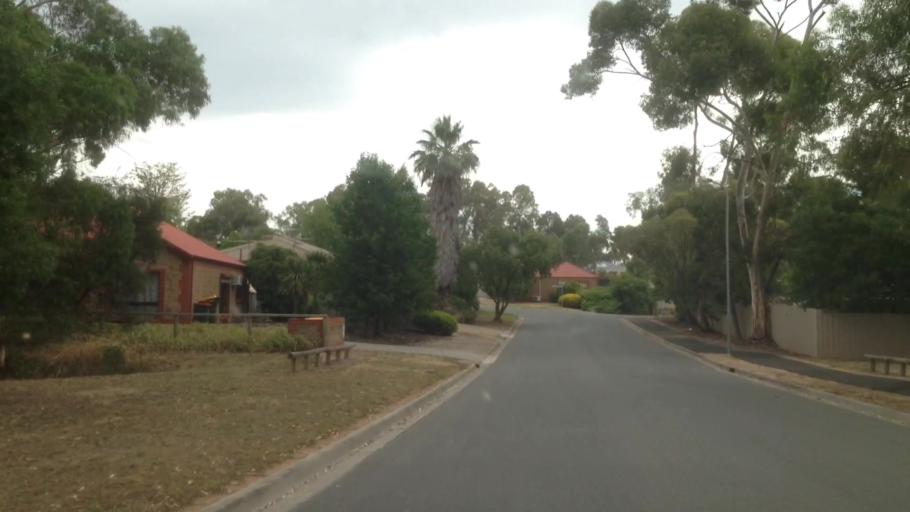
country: AU
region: South Australia
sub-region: Barossa
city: Williamstown
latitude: -34.6687
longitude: 138.8868
